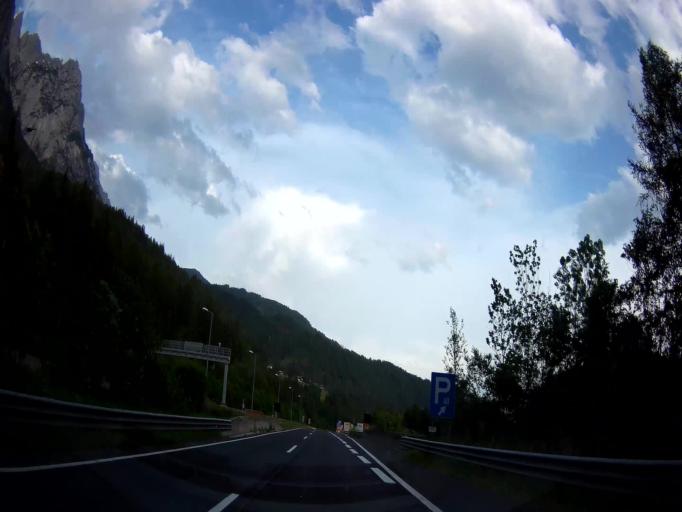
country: AT
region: Salzburg
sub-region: Politischer Bezirk Sankt Johann im Pongau
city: Werfen
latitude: 47.4910
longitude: 13.1839
